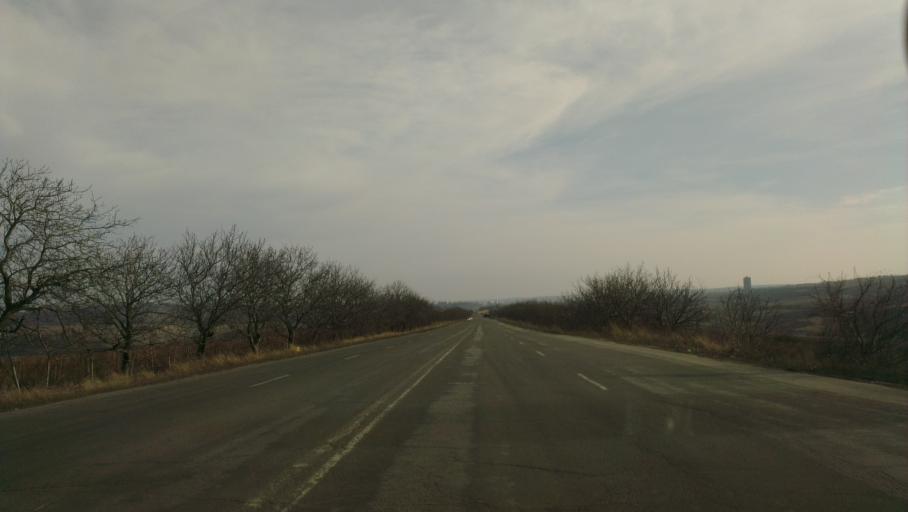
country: MD
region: Laloveni
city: Ialoveni
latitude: 46.9981
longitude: 28.7340
